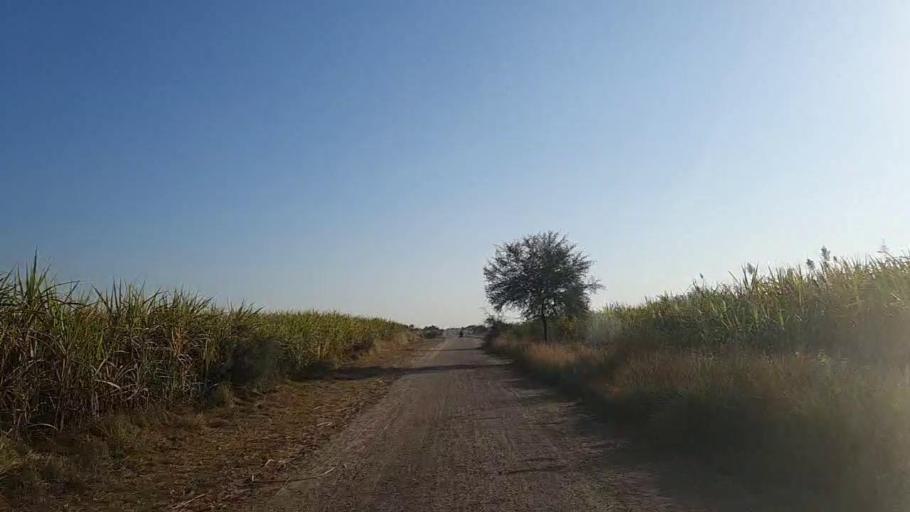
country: PK
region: Sindh
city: Khadro
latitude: 26.2685
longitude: 68.8602
